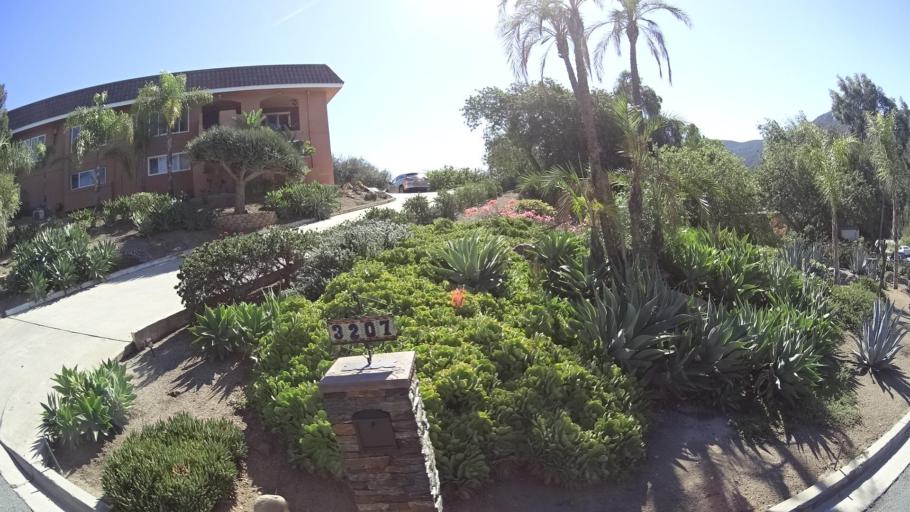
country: US
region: California
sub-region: San Diego County
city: Jamul
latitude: 32.7296
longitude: -116.9065
